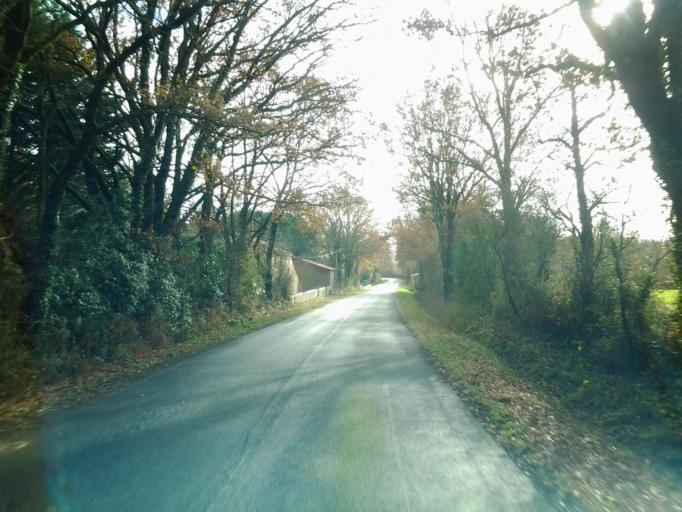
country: FR
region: Pays de la Loire
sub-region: Departement de la Vendee
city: Saint-Florent-des-Bois
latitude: 46.6265
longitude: -1.3017
